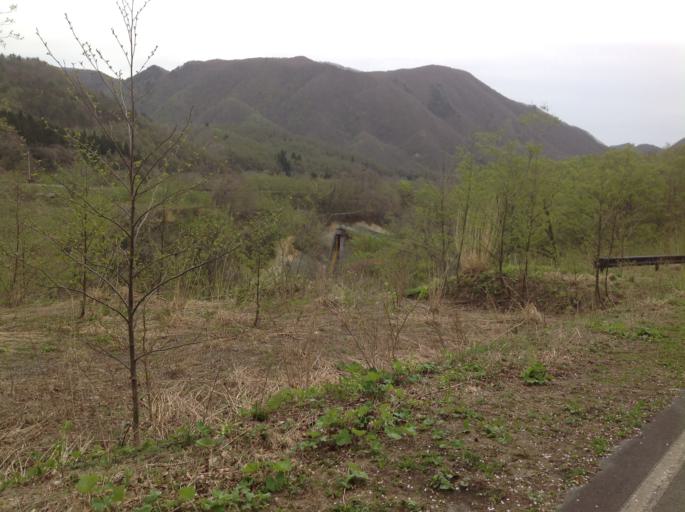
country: JP
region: Iwate
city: Ichinoseki
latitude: 39.0151
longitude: 140.8766
